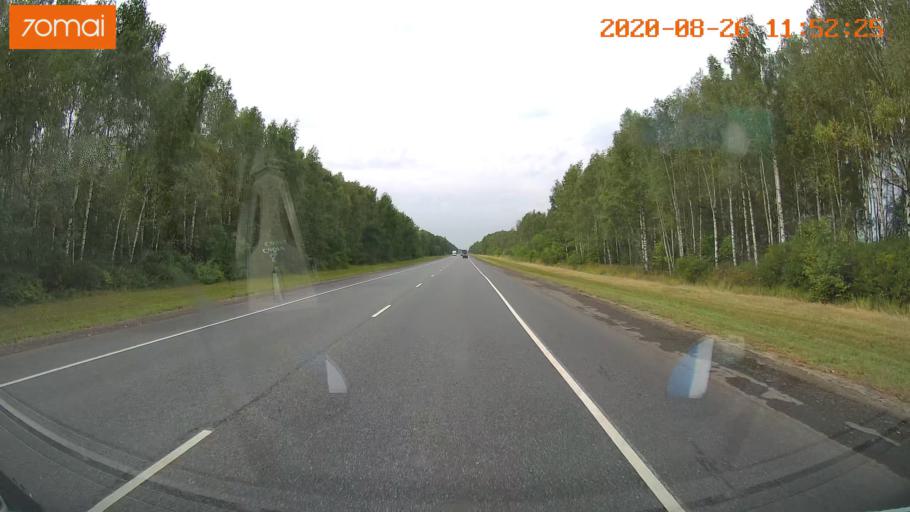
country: RU
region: Rjazan
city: Lesnoy
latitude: 54.2942
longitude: 40.4553
